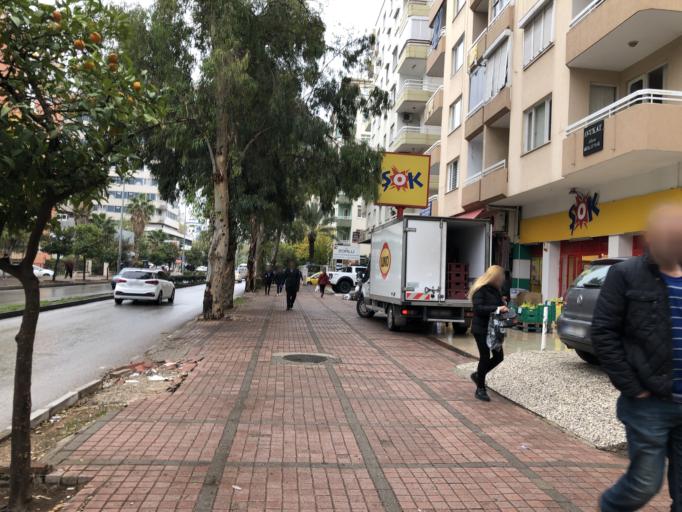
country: TR
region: Antalya
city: Antalya
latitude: 36.8940
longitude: 30.6929
